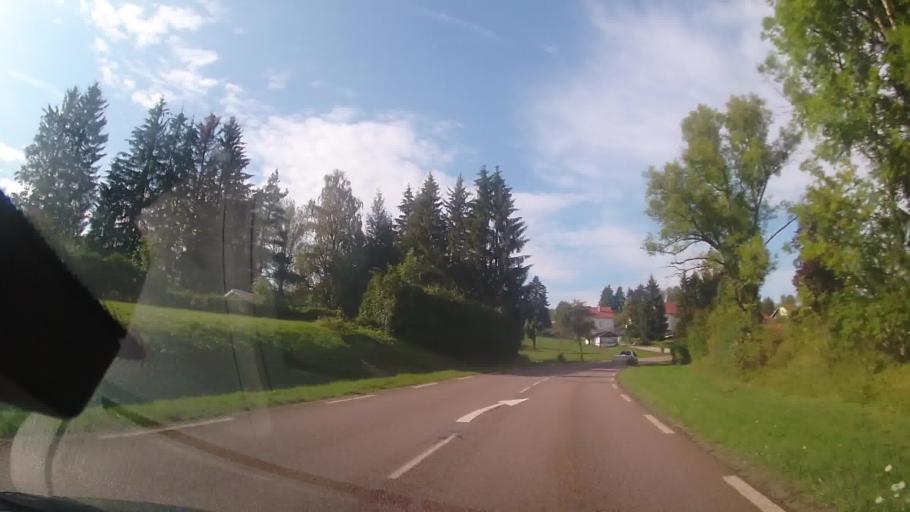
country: FR
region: Franche-Comte
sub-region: Departement du Jura
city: Morbier
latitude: 46.6013
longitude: 5.9027
